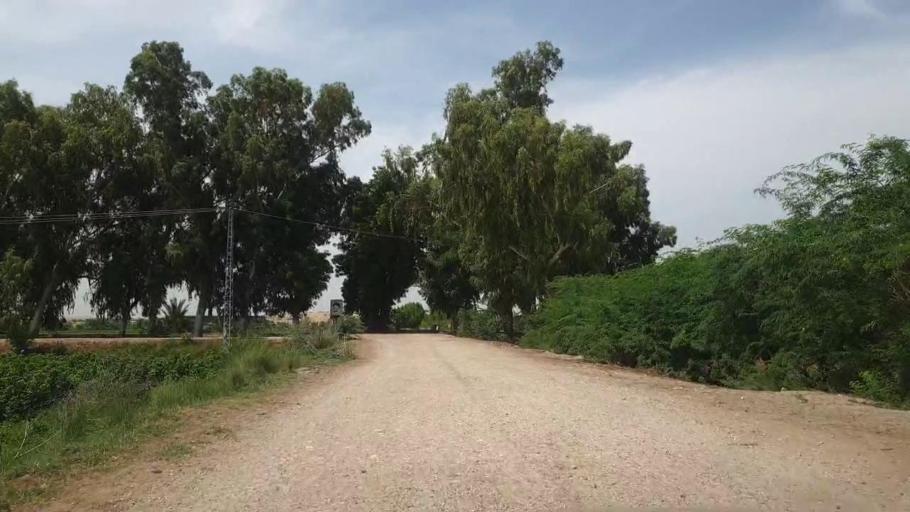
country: PK
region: Sindh
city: Kot Diji
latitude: 27.1232
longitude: 68.9986
